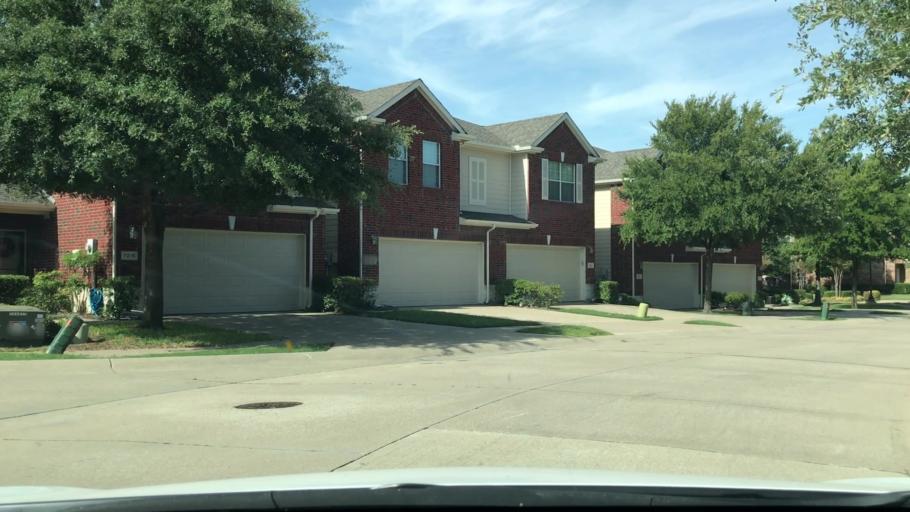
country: US
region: Texas
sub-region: Denton County
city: The Colony
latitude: 33.0455
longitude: -96.8573
